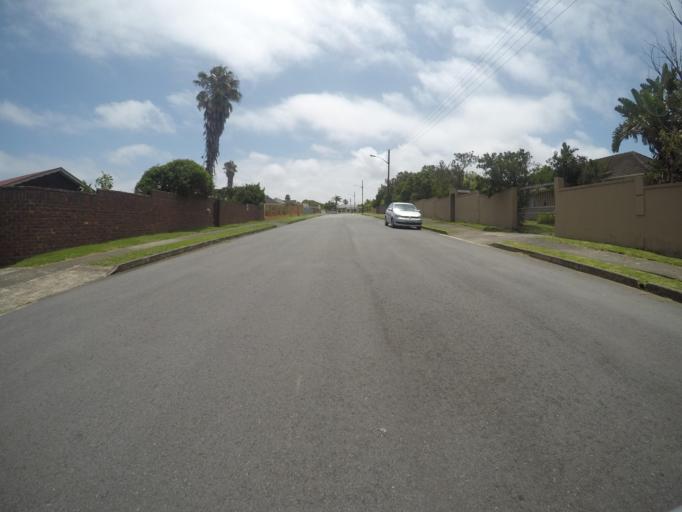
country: ZA
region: Eastern Cape
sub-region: Buffalo City Metropolitan Municipality
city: East London
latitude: -33.0000
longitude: 27.9200
